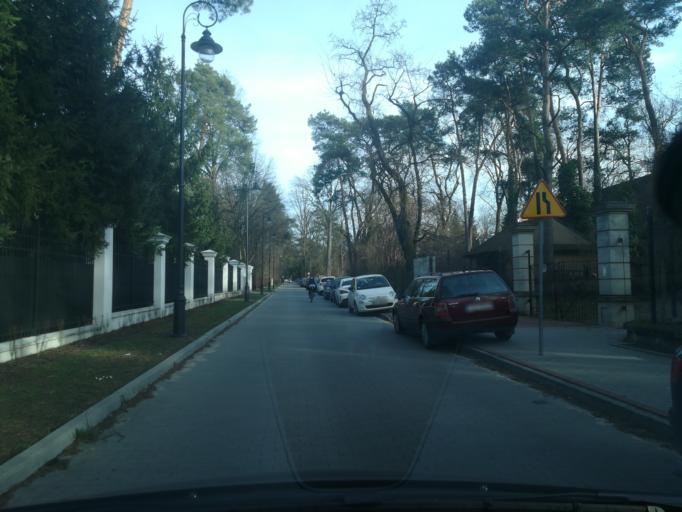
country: PL
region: Masovian Voivodeship
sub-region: Powiat piaseczynski
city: Konstancin-Jeziorna
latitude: 52.0848
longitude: 21.1220
